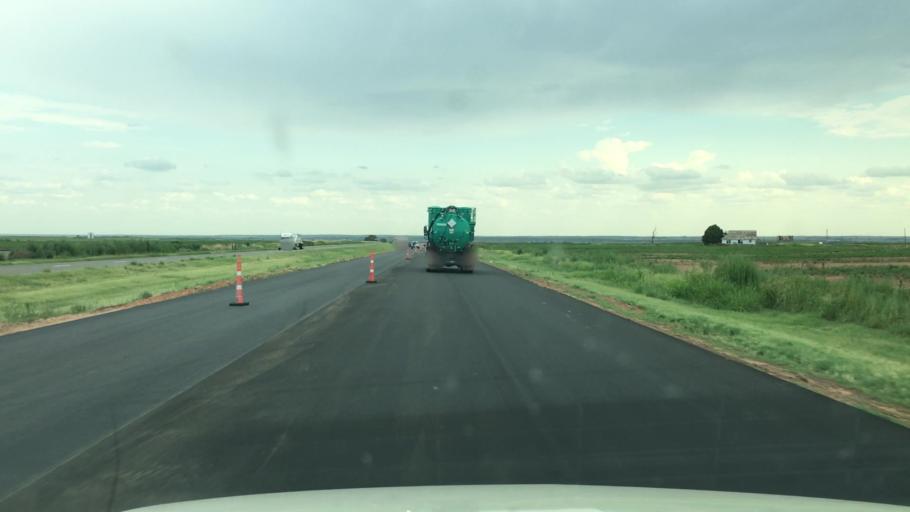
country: US
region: Texas
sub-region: Hall County
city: Memphis
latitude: 34.6177
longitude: -100.4713
